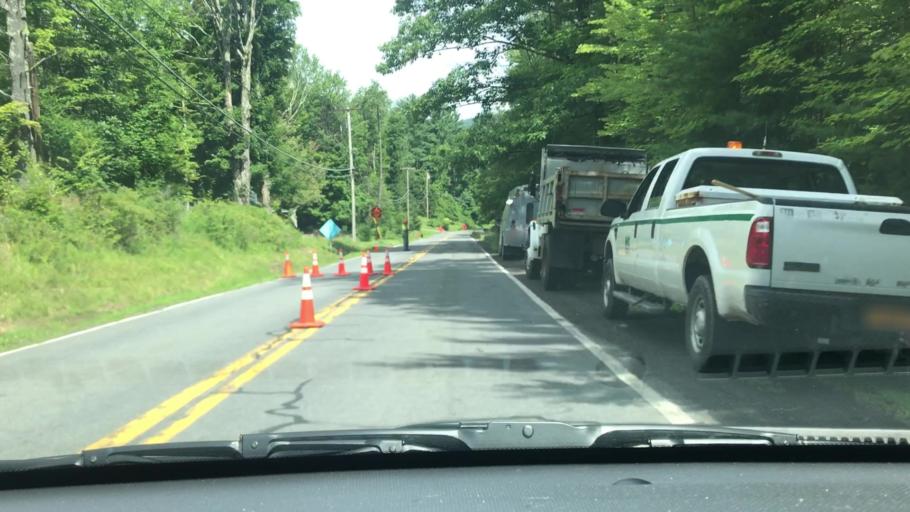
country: US
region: New York
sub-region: Ulster County
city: Shokan
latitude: 41.9848
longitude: -74.2745
